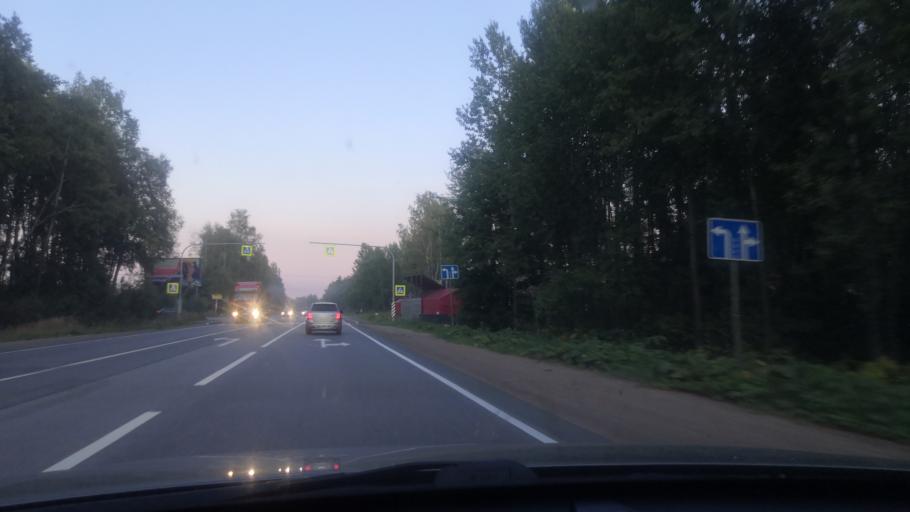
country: RU
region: St.-Petersburg
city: Beloostrov
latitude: 60.1984
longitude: 30.0053
